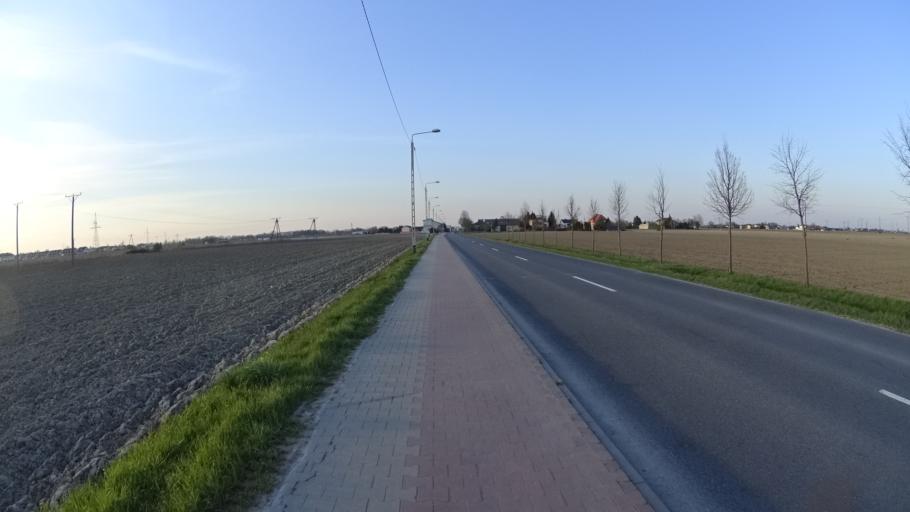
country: PL
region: Masovian Voivodeship
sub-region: Powiat warszawski zachodni
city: Ozarow Mazowiecki
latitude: 52.2184
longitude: 20.8122
